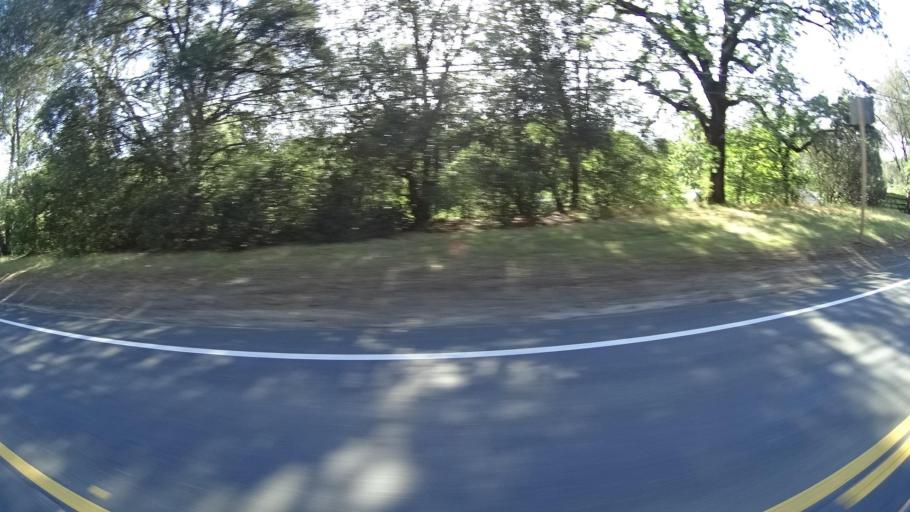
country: US
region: California
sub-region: Lake County
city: Upper Lake
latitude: 39.1533
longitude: -122.9207
